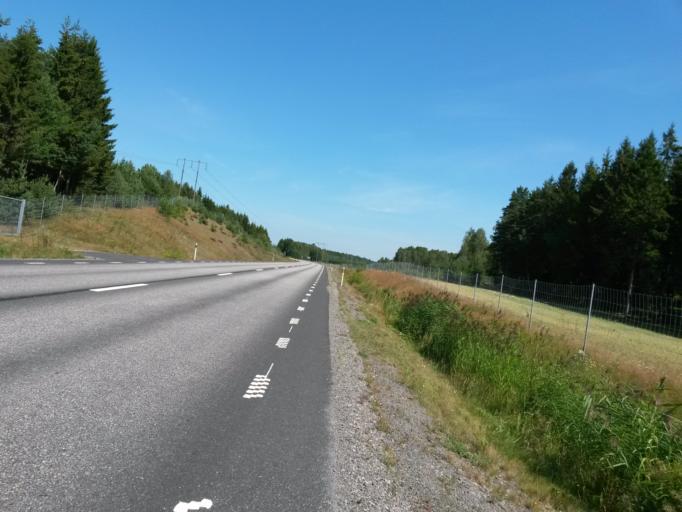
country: SE
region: Vaestra Goetaland
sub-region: Vara Kommun
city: Vara
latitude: 58.4460
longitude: 12.9717
